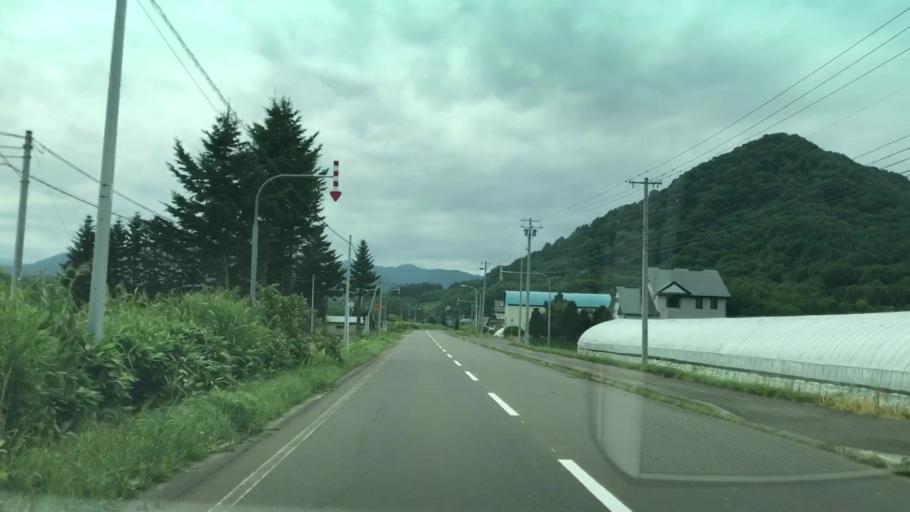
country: JP
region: Hokkaido
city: Yoichi
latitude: 43.0773
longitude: 140.8162
